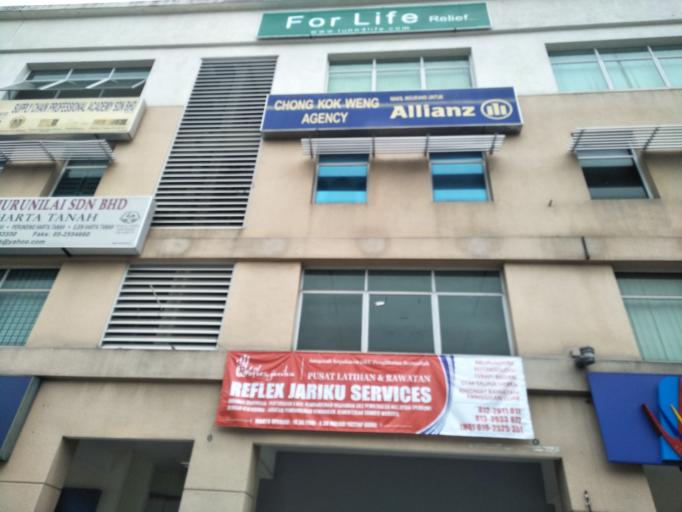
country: MY
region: Perak
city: Ipoh
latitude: 4.6006
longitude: 101.0940
